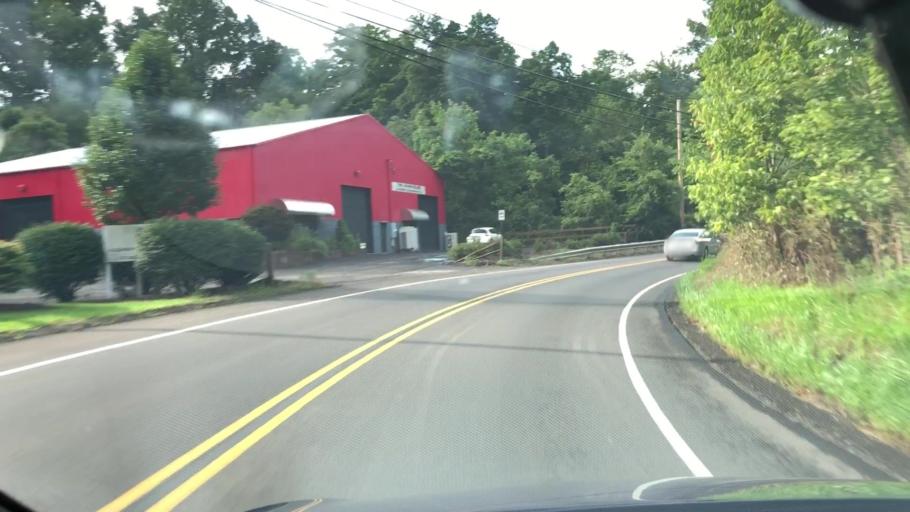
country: US
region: Pennsylvania
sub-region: Washington County
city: Thompsonville
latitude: 40.2929
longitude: -80.1060
